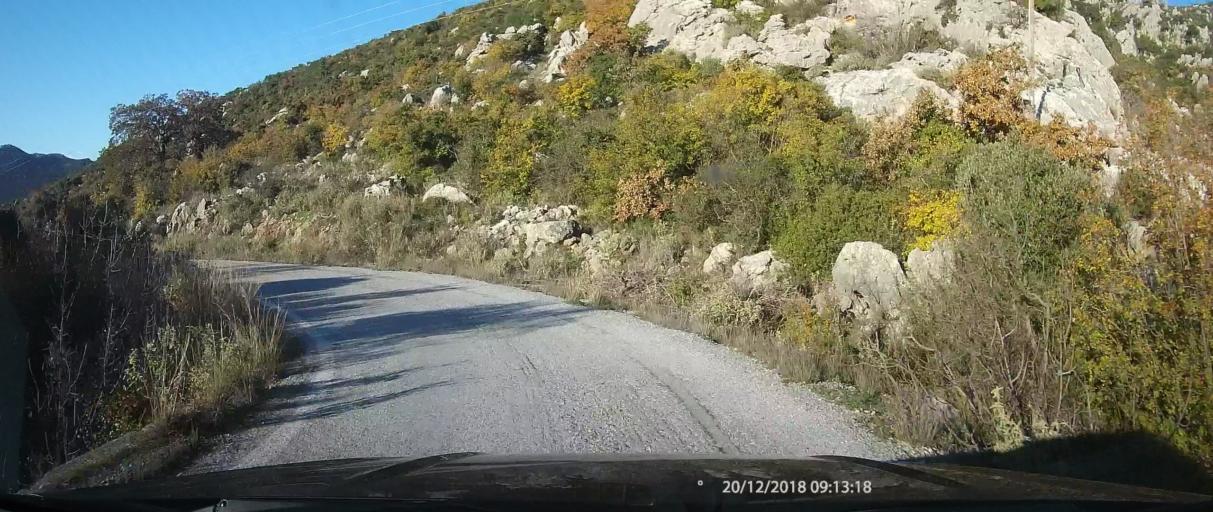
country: GR
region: Peloponnese
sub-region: Nomos Lakonias
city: Sykea
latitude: 36.9034
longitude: 22.9950
